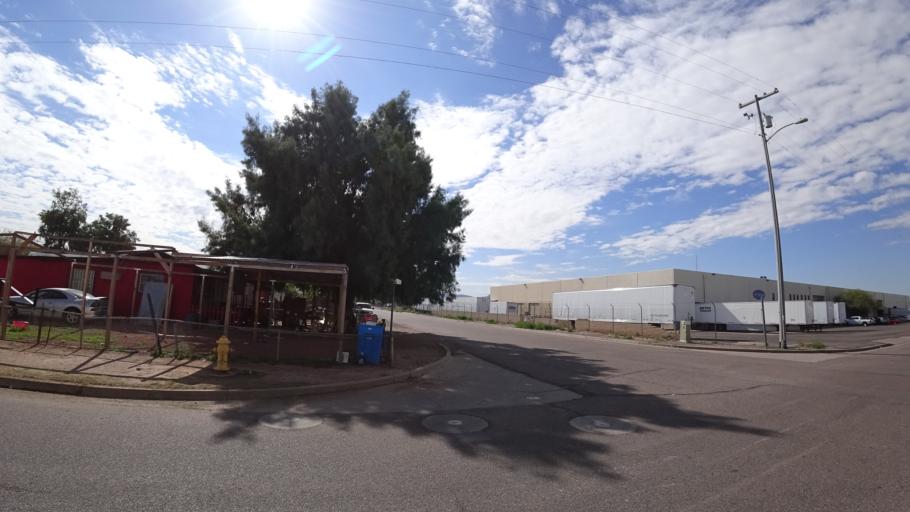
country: US
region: Arizona
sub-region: Maricopa County
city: Phoenix
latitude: 33.4332
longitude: -112.0694
